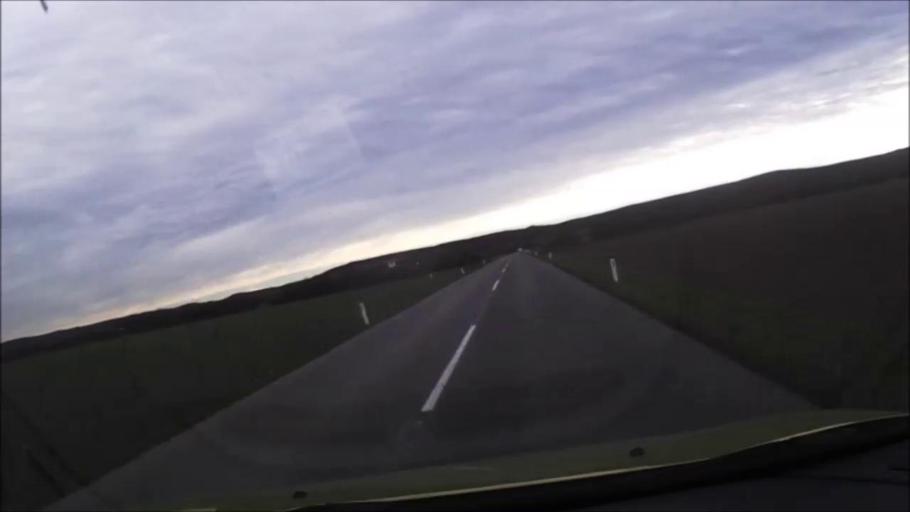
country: AT
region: Burgenland
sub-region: Eisenstadt-Umgebung
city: Leithaprodersdorf
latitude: 47.9273
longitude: 16.4988
